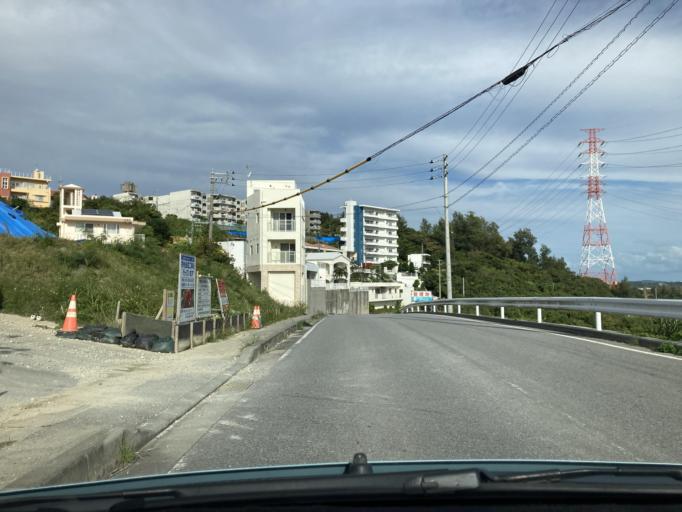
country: JP
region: Okinawa
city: Okinawa
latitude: 26.3399
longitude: 127.8306
